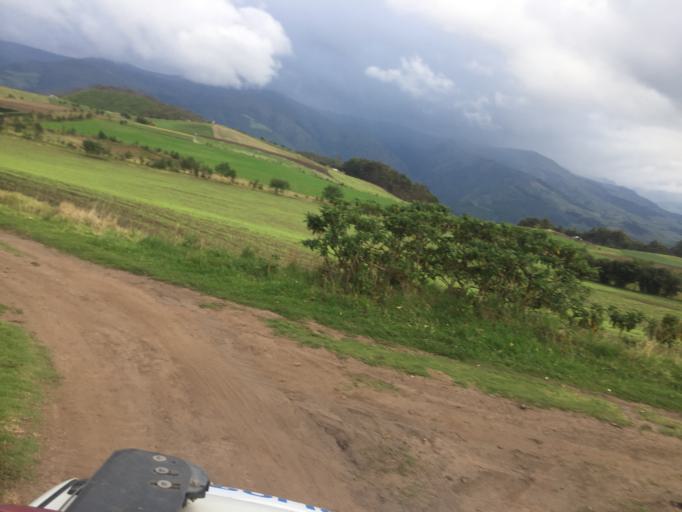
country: EC
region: Imbabura
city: Ibarra
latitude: 0.2259
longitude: -78.1200
